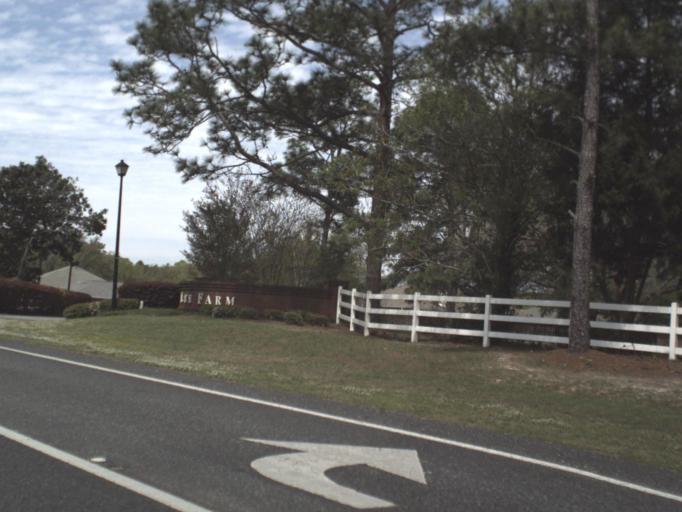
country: US
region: Florida
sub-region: Okaloosa County
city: Crestview
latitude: 30.7649
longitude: -86.6005
